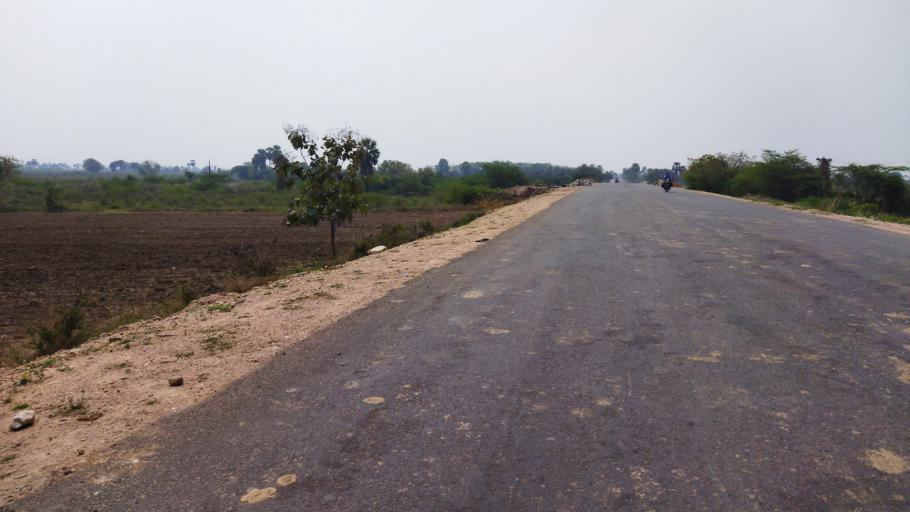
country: IN
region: Telangana
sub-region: Nalgonda
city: Nalgonda
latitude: 17.1028
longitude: 79.3444
